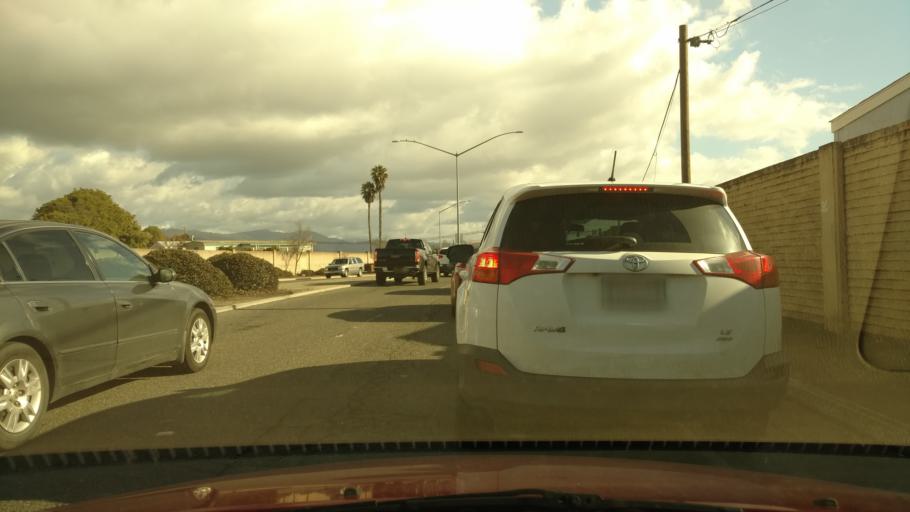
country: US
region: California
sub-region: Monterey County
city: Boronda
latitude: 36.7210
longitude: -121.6527
